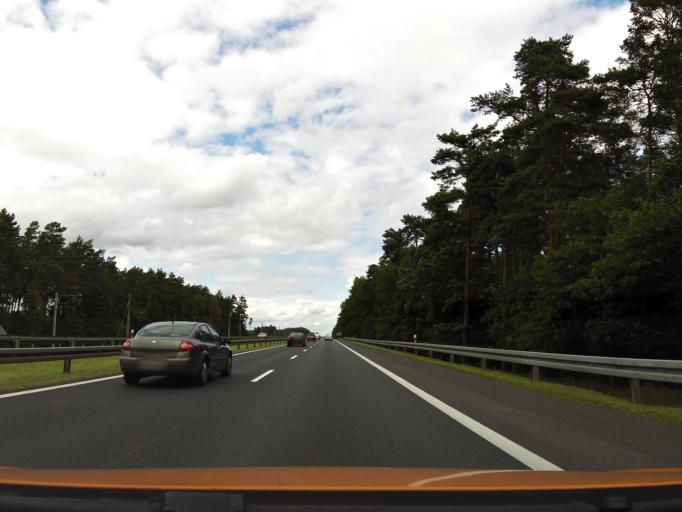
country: PL
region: West Pomeranian Voivodeship
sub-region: Powiat goleniowski
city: Goleniow
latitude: 53.5026
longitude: 14.7997
